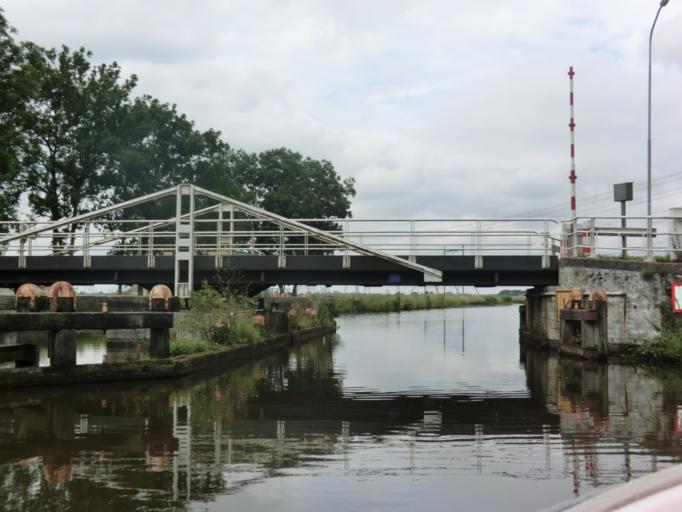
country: NL
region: Groningen
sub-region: Gemeente Appingedam
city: Appingedam
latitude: 53.2902
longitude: 6.8381
